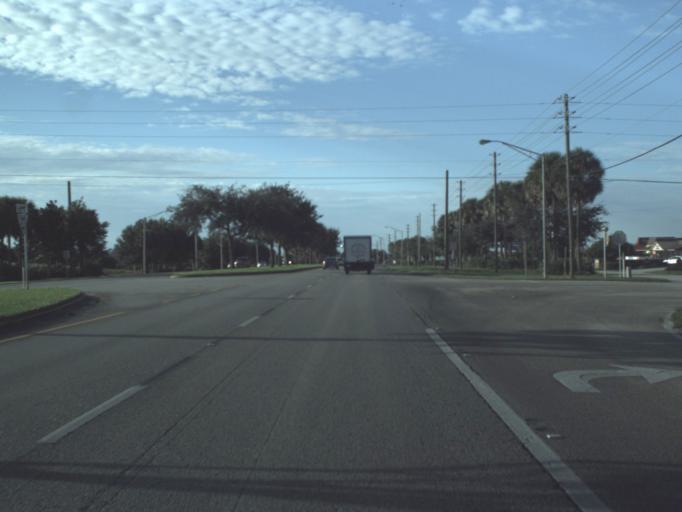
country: US
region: Florida
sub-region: Highlands County
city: Lake Placid
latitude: 27.2931
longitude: -81.3585
